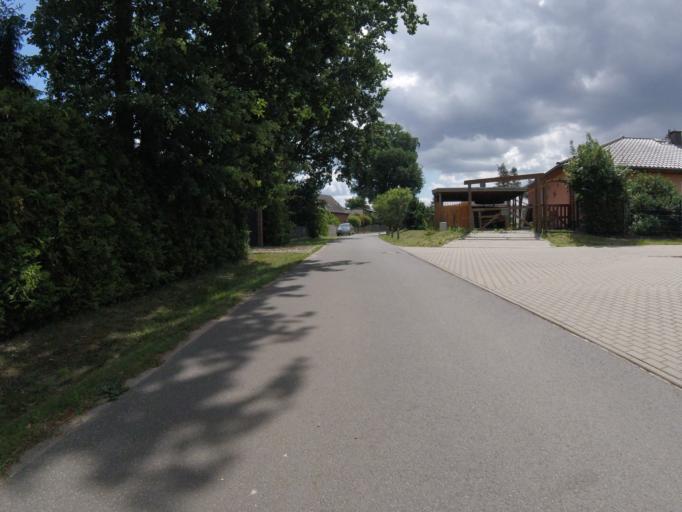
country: DE
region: Brandenburg
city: Bestensee
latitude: 52.2351
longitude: 13.6214
